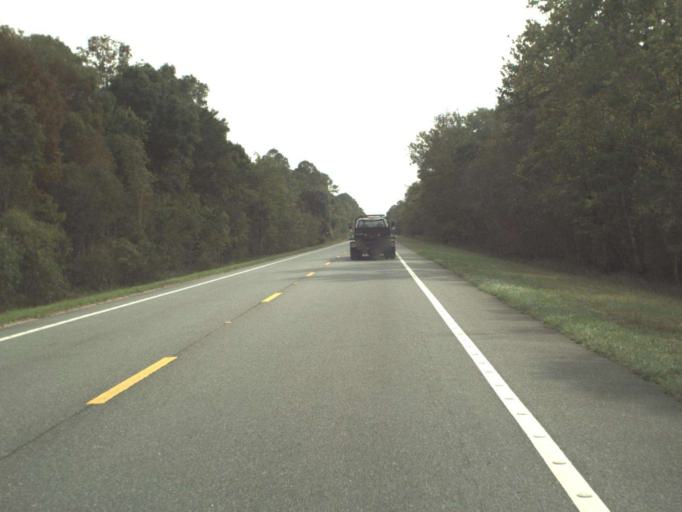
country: US
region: Florida
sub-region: Leon County
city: Woodville
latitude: 30.1734
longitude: -84.0086
